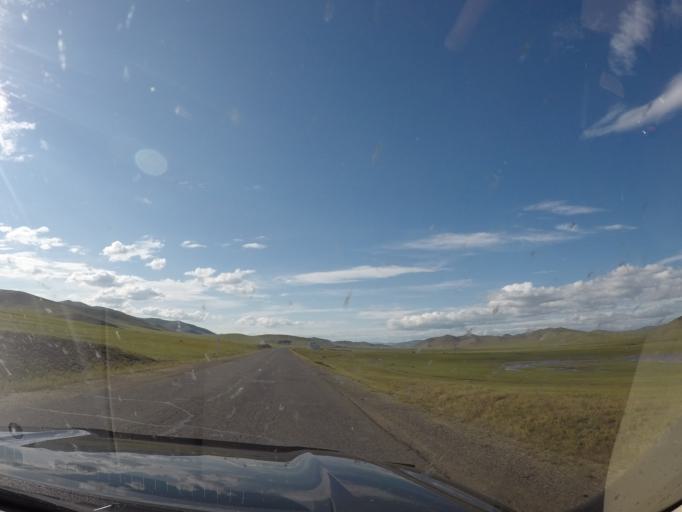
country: MN
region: Hentiy
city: Modot
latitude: 47.7292
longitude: 109.0153
